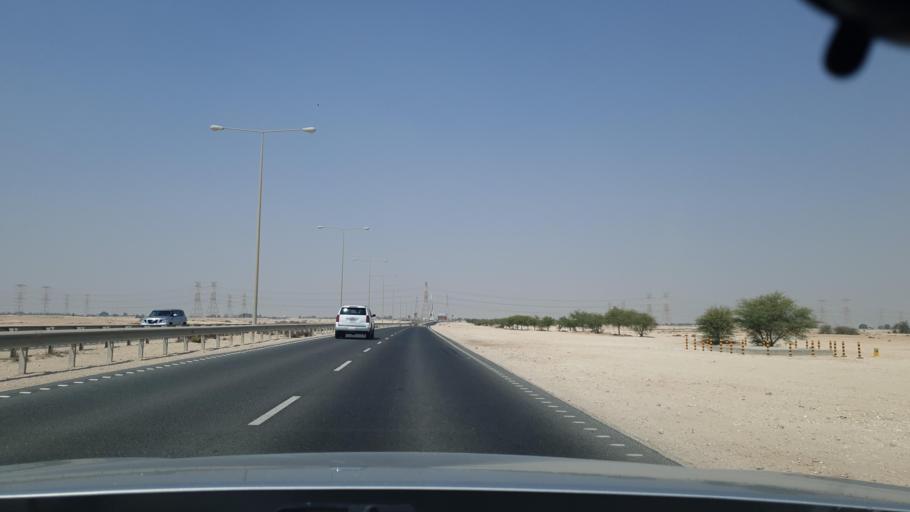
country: QA
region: Al Khawr
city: Al Khawr
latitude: 25.7478
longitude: 51.4801
